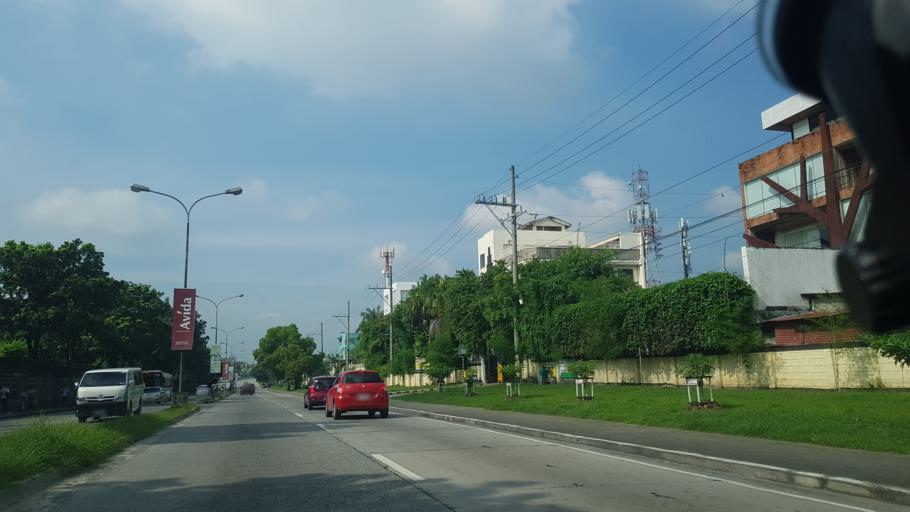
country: PH
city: Sambayanihan People's Village
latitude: 14.4177
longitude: 121.0194
